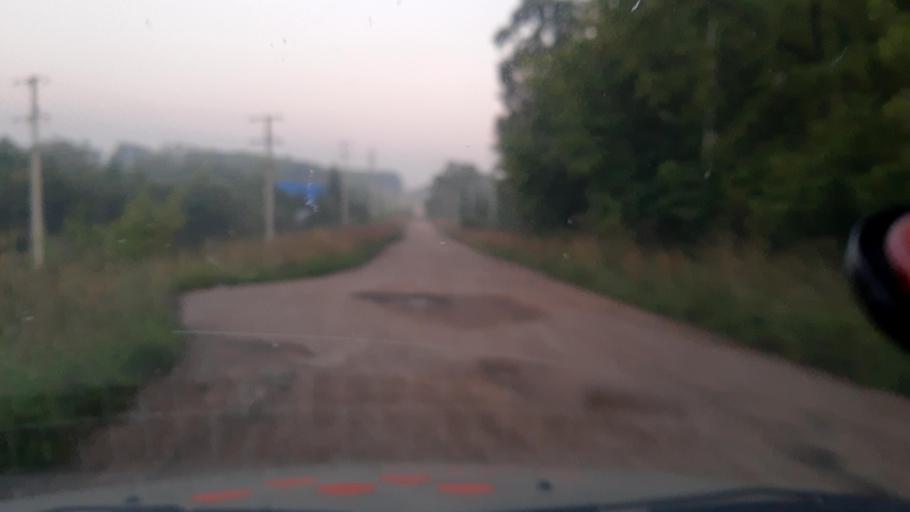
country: RU
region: Bashkortostan
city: Blagoveshchensk
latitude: 55.0509
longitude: 55.9814
